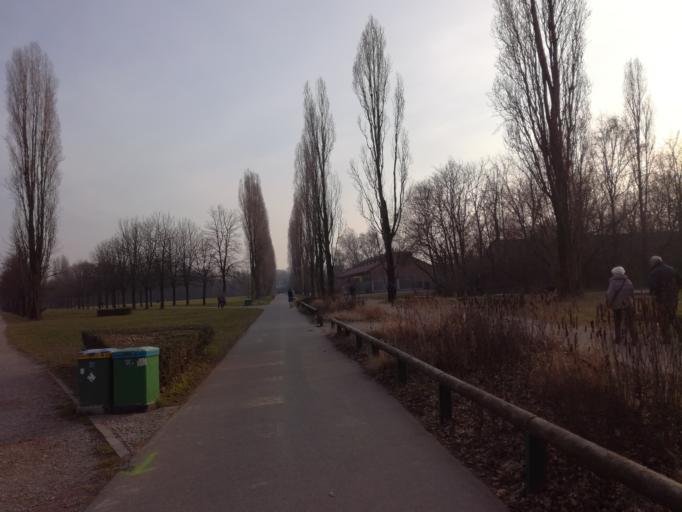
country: IT
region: Lombardy
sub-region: Citta metropolitana di Milano
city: Cinisello Balsamo
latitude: 45.5392
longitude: 9.2101
